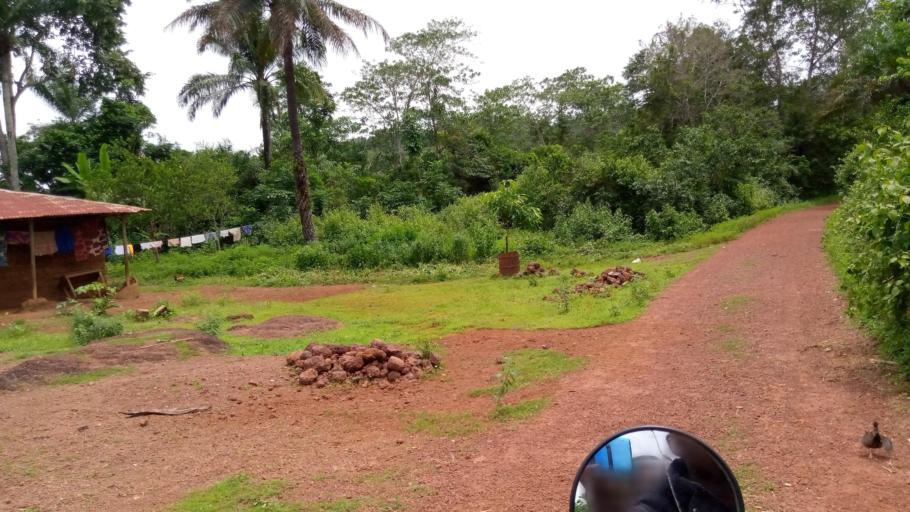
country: SL
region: Southern Province
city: Rotifunk
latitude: 8.1952
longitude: -12.5682
